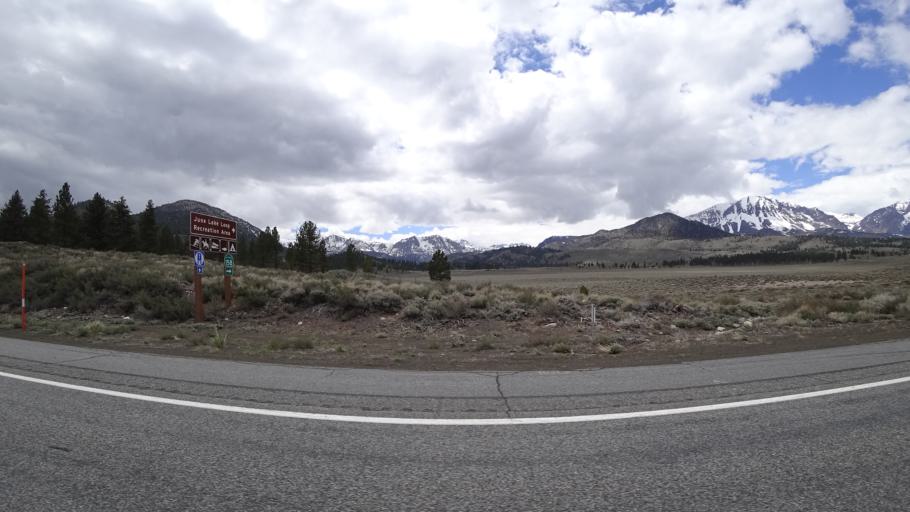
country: US
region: California
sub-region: Mono County
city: Mammoth Lakes
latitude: 37.8144
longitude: -119.0557
